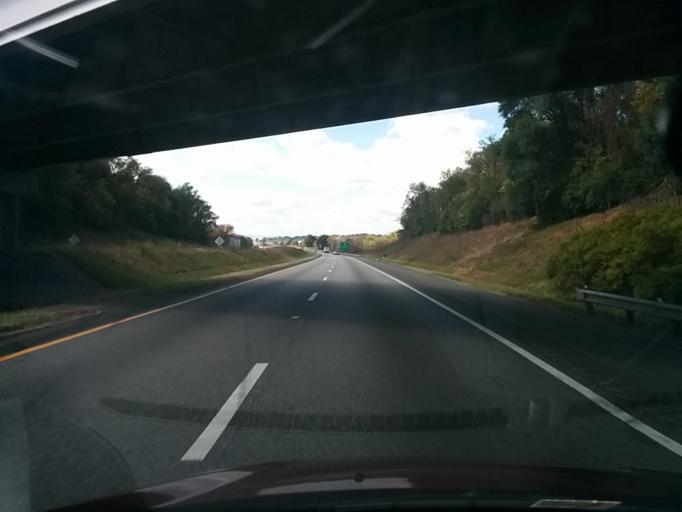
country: US
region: Virginia
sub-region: City of Waynesboro
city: Waynesboro
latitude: 38.0537
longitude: -78.9185
